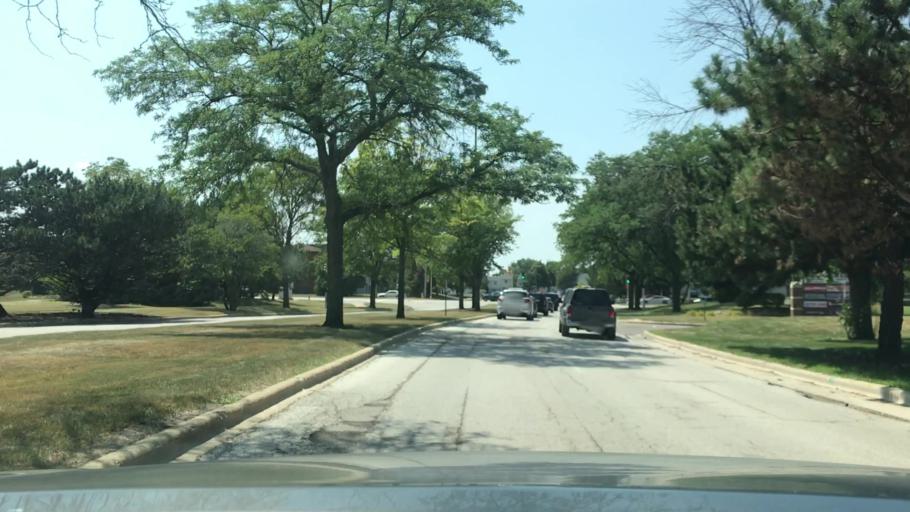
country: US
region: Illinois
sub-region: DuPage County
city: Warrenville
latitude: 41.7583
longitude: -88.2181
